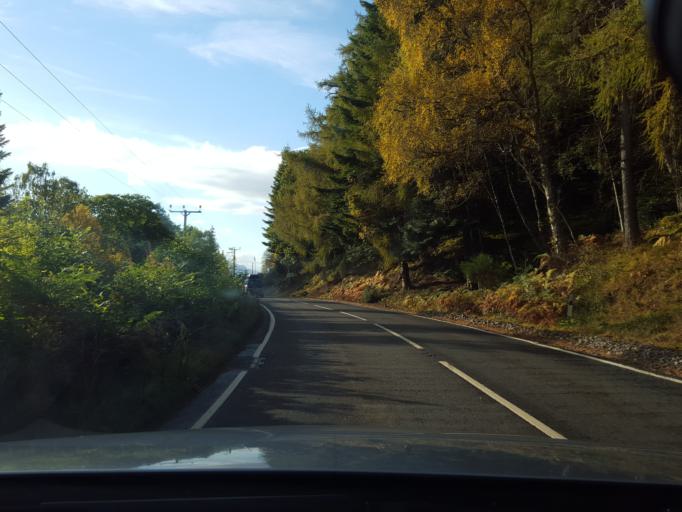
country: GB
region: Scotland
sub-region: Highland
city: Beauly
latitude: 57.2381
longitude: -4.5563
